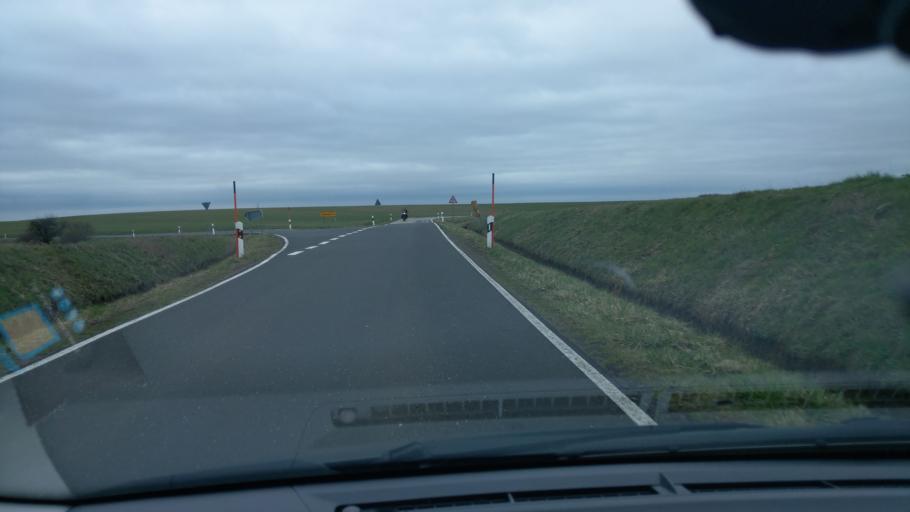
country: DE
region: Rheinland-Pfalz
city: Kleinbundenbach
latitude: 49.3187
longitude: 7.4374
